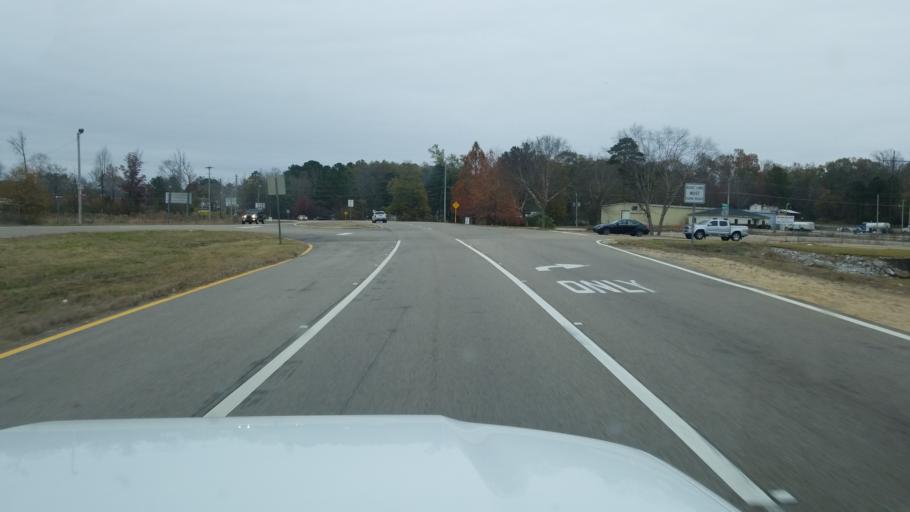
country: US
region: Mississippi
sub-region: Lee County
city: Tupelo
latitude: 34.2882
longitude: -88.6767
